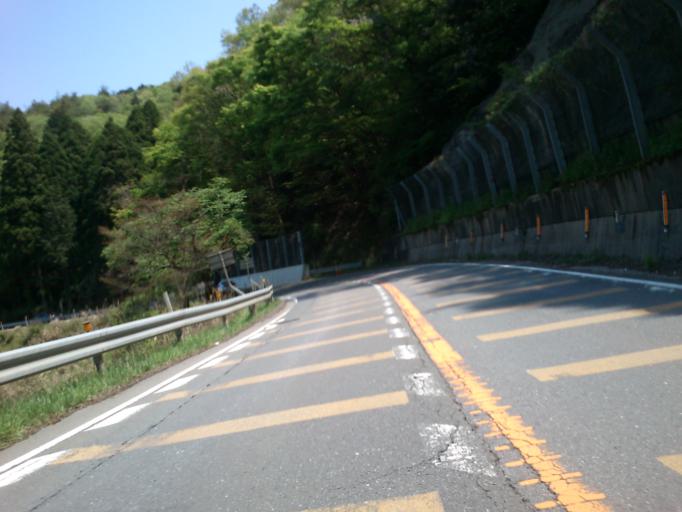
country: JP
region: Kyoto
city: Kameoka
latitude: 35.1225
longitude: 135.4514
